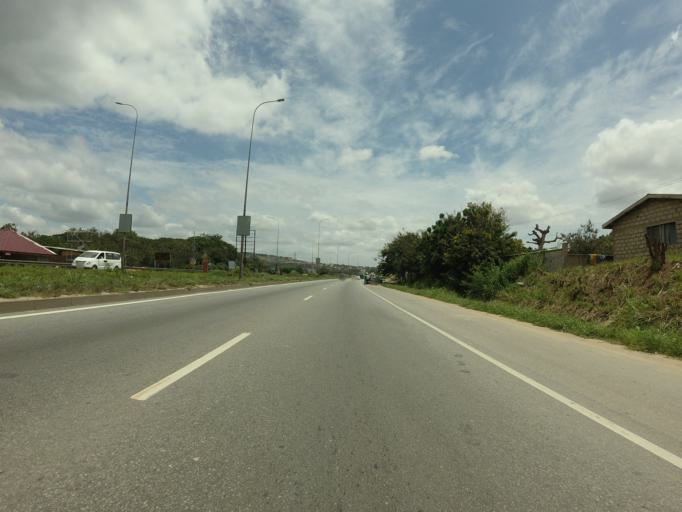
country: GH
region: Central
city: Kasoa
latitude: 5.5494
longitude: -0.3767
